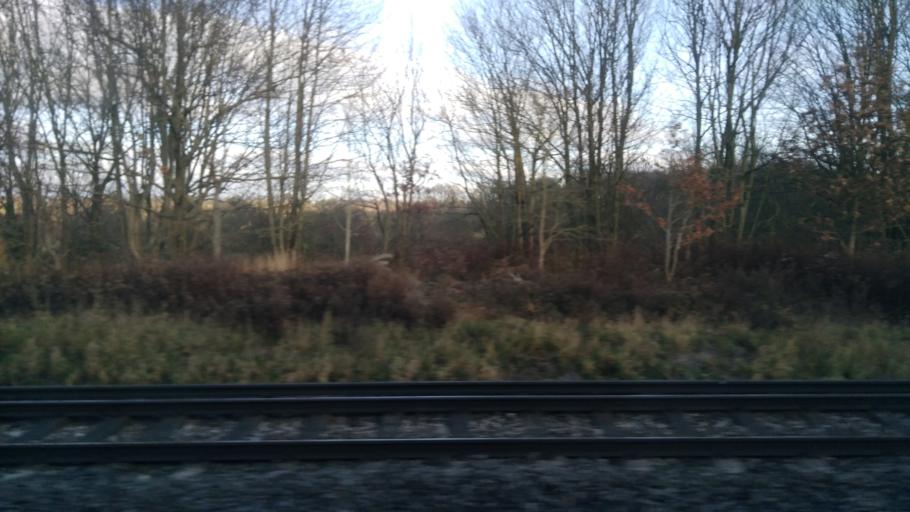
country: GB
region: England
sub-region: Greater London
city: Chislehurst
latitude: 51.3973
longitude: 0.0658
